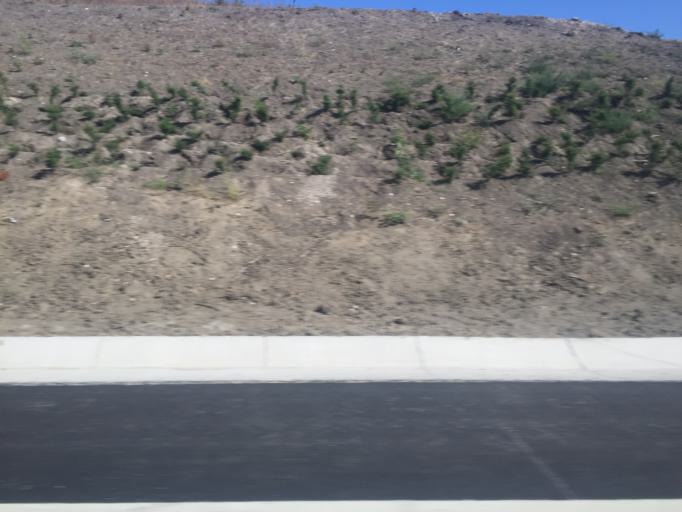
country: TR
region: Bursa
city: Mahmudiye
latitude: 40.2570
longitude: 28.7239
